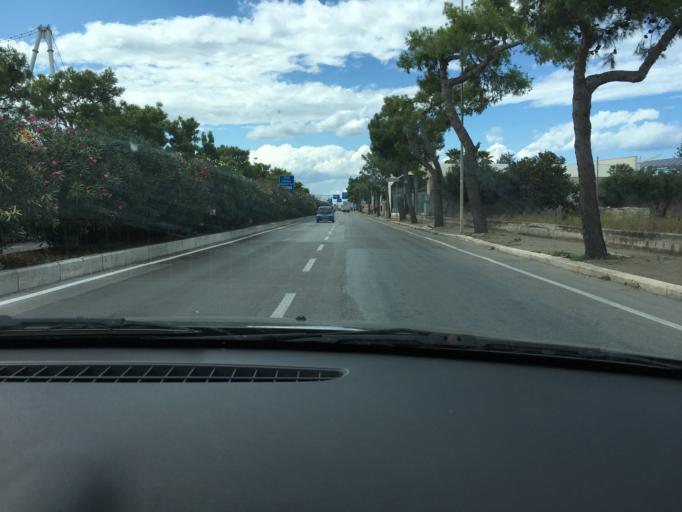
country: IT
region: Apulia
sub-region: Provincia di Bari
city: San Paolo
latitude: 41.1334
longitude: 16.8212
